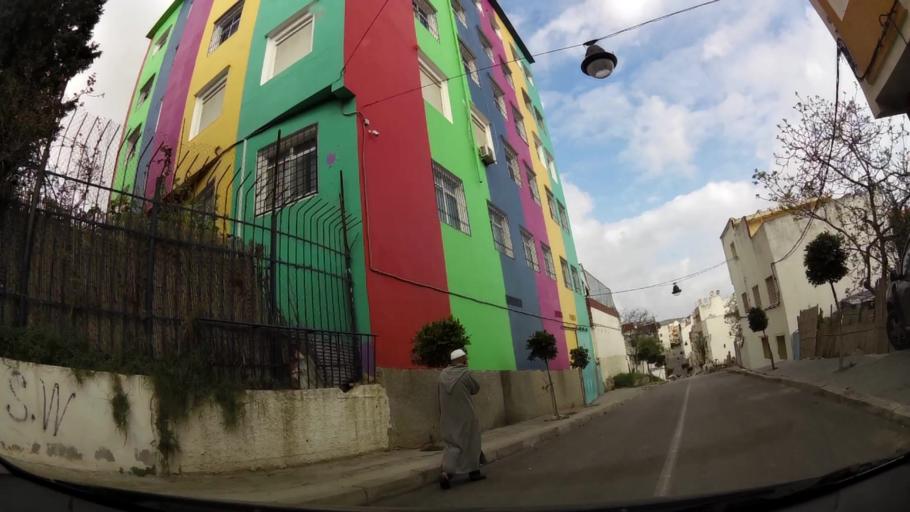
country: MA
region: Tanger-Tetouan
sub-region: Tanger-Assilah
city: Tangier
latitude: 35.7624
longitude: -5.8269
